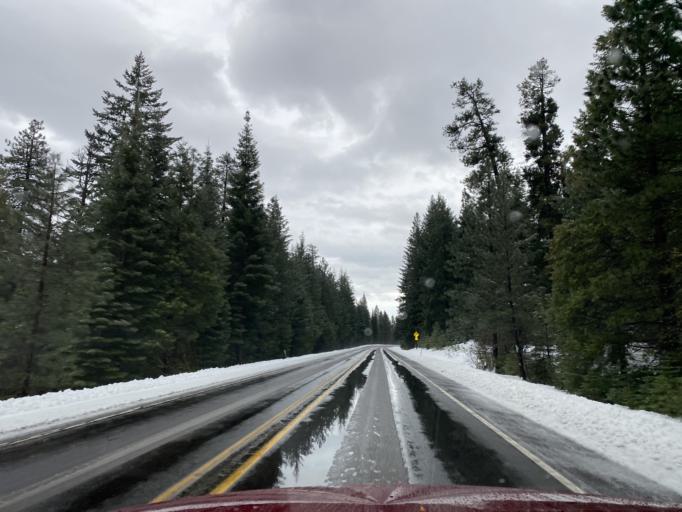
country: US
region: Oregon
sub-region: Klamath County
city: Klamath Falls
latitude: 42.5241
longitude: -122.0869
